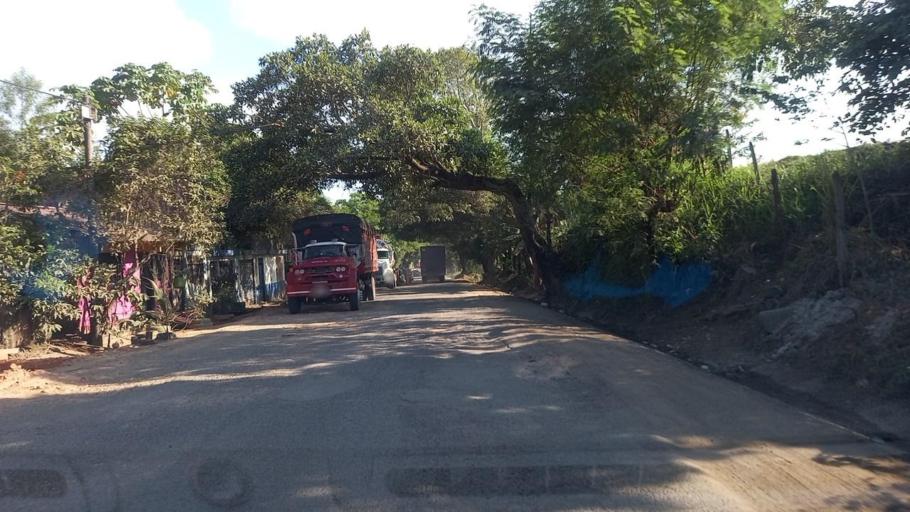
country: CO
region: Boyaca
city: Puerto Boyaca
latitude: 5.9324
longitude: -74.5690
